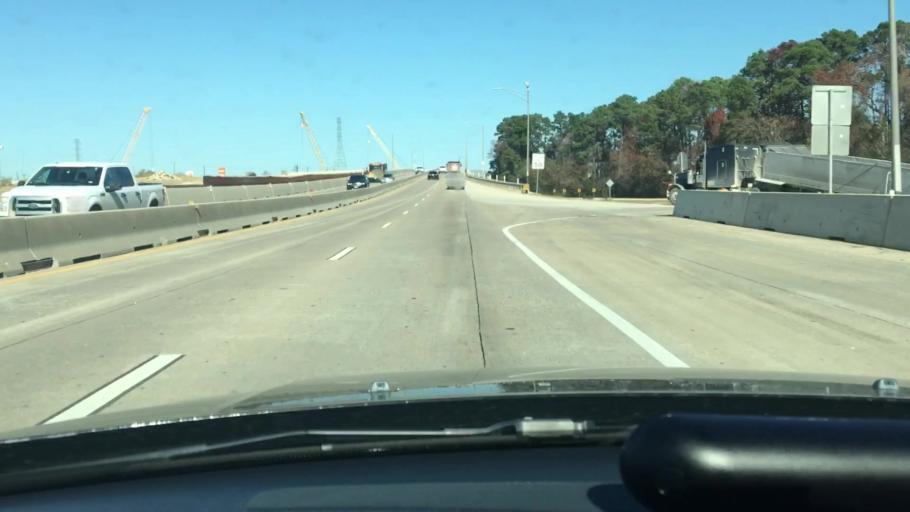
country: US
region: Texas
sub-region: Harris County
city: Cloverleaf
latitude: 29.7514
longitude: -95.1458
